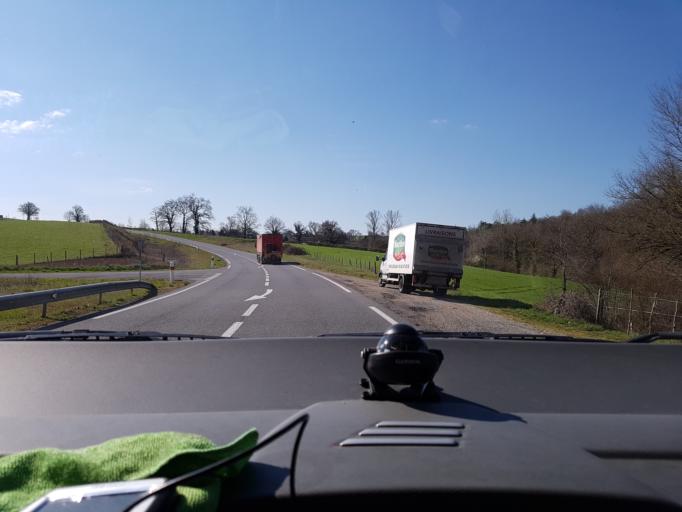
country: FR
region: Midi-Pyrenees
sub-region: Departement de l'Aveyron
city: Moyrazes
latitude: 44.3763
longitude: 2.4590
